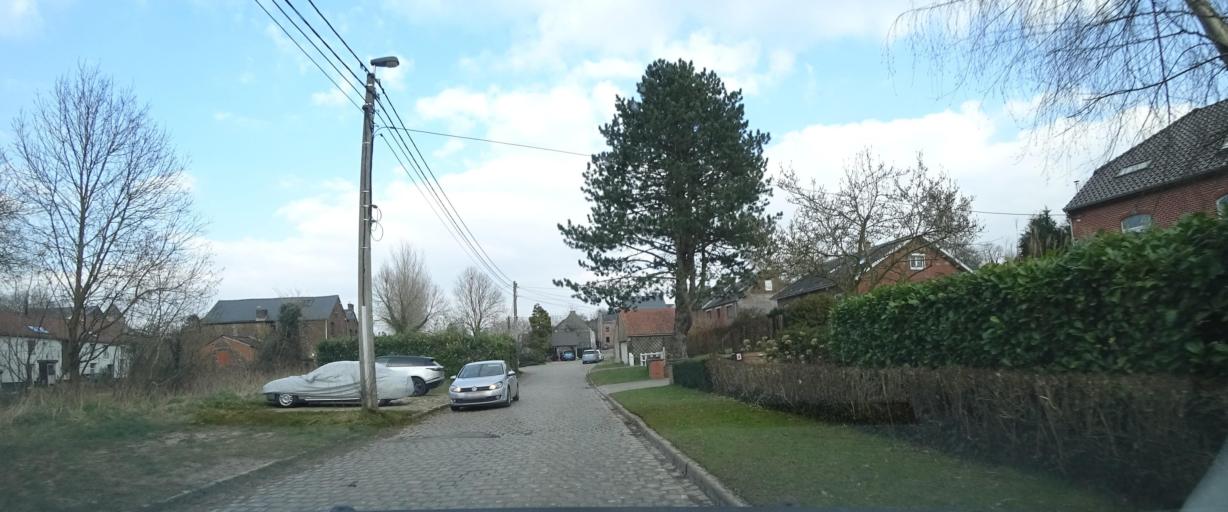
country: BE
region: Wallonia
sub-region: Province du Brabant Wallon
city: Walhain-Saint-Paul
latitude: 50.6666
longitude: 4.6716
